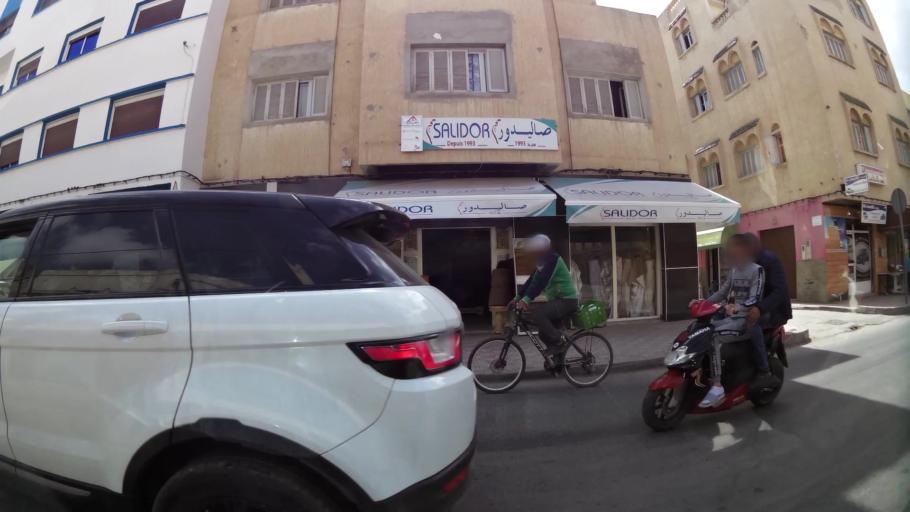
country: MA
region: Oriental
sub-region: Nador
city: Nador
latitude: 35.1671
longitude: -2.9309
